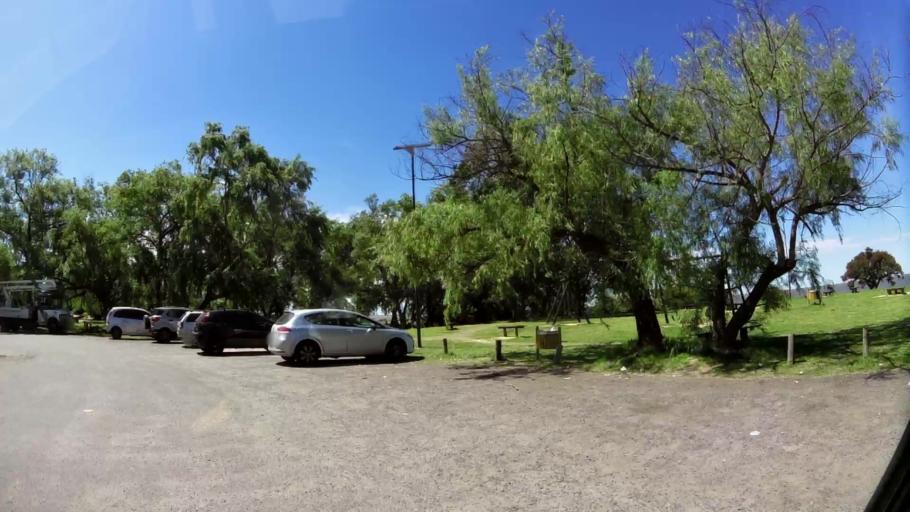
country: AR
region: Buenos Aires
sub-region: Partido de San Isidro
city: San Isidro
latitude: -34.4780
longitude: -58.4843
